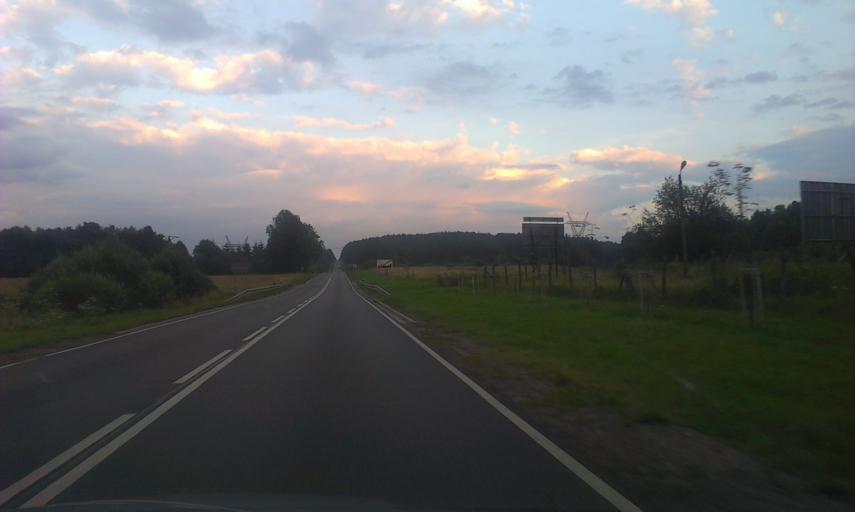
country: PL
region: West Pomeranian Voivodeship
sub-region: Powiat koszalinski
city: Sianow
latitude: 54.1226
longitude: 16.3069
